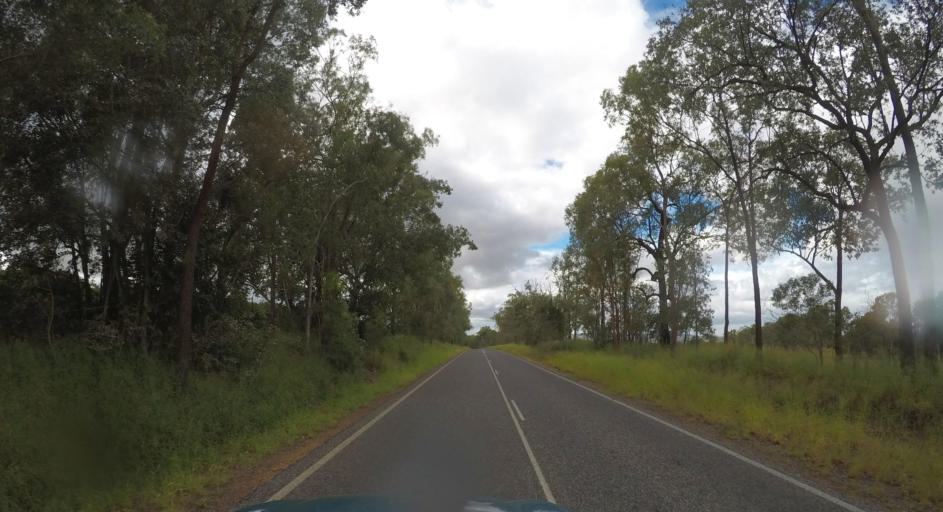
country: AU
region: Queensland
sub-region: North Burnett
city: Gayndah
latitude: -25.6270
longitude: 151.2863
